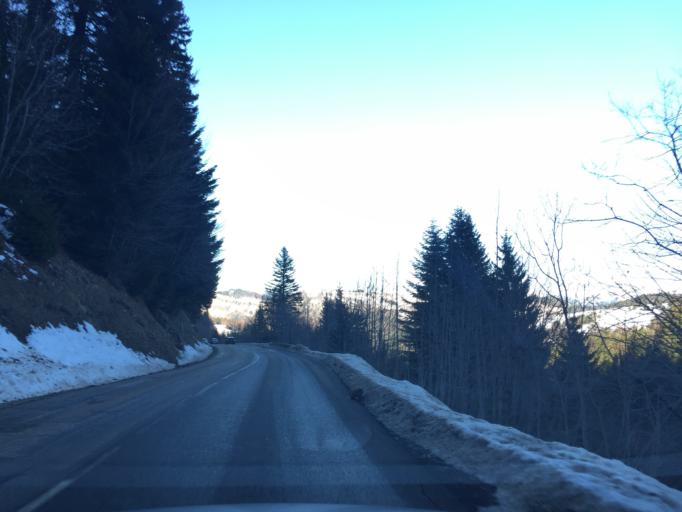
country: FR
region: Rhone-Alpes
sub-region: Departement de la Savoie
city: Mouxy
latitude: 45.6836
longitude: 5.9960
